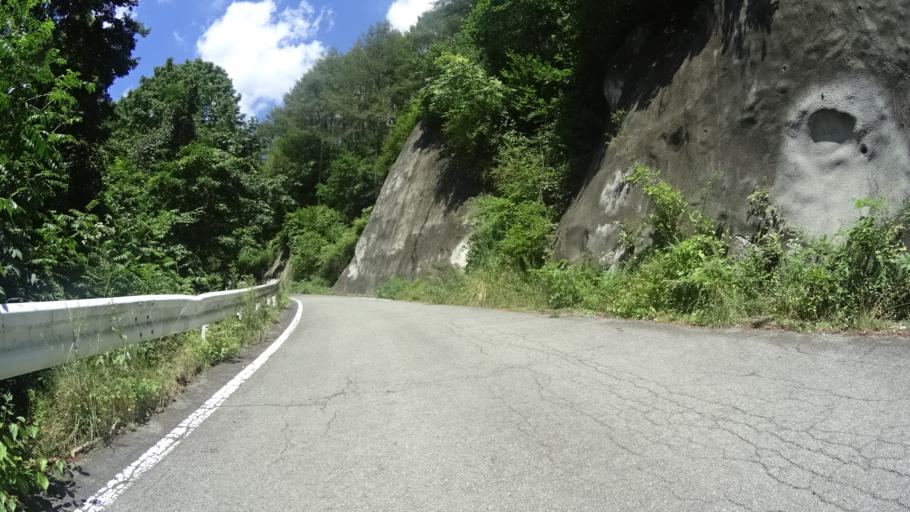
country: JP
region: Yamanashi
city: Enzan
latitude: 35.8190
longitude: 138.6540
